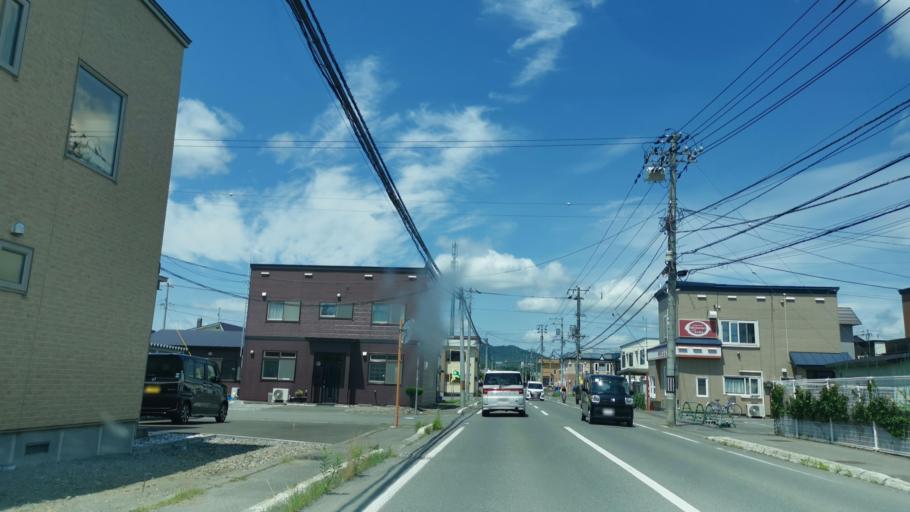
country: JP
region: Hokkaido
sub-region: Asahikawa-shi
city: Asahikawa
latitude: 43.7902
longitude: 142.3384
